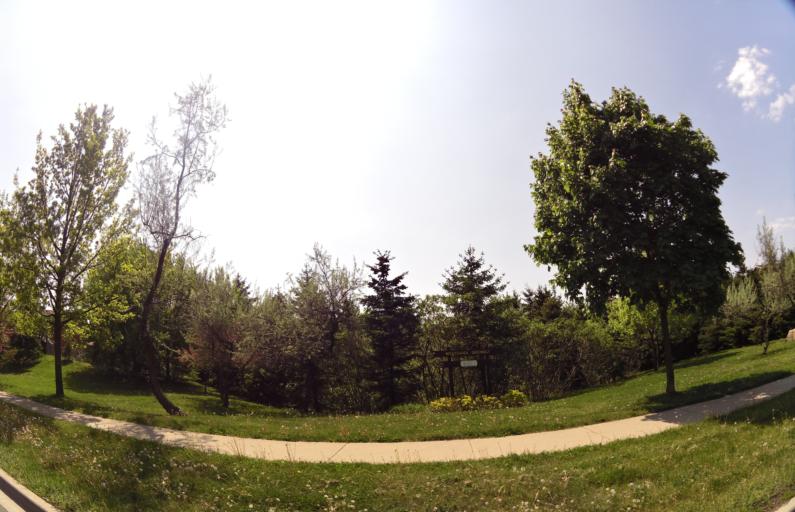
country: CA
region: Ontario
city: Mississauga
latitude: 43.6115
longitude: -79.6397
